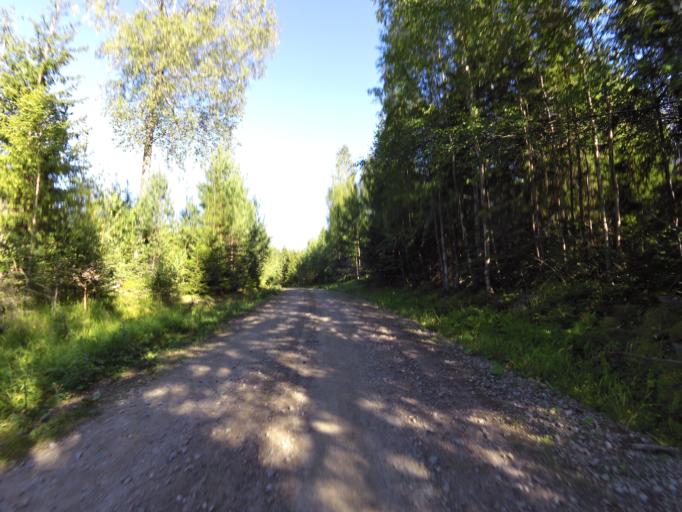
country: SE
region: Gaevleborg
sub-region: Hofors Kommun
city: Hofors
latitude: 60.6508
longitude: 16.2623
